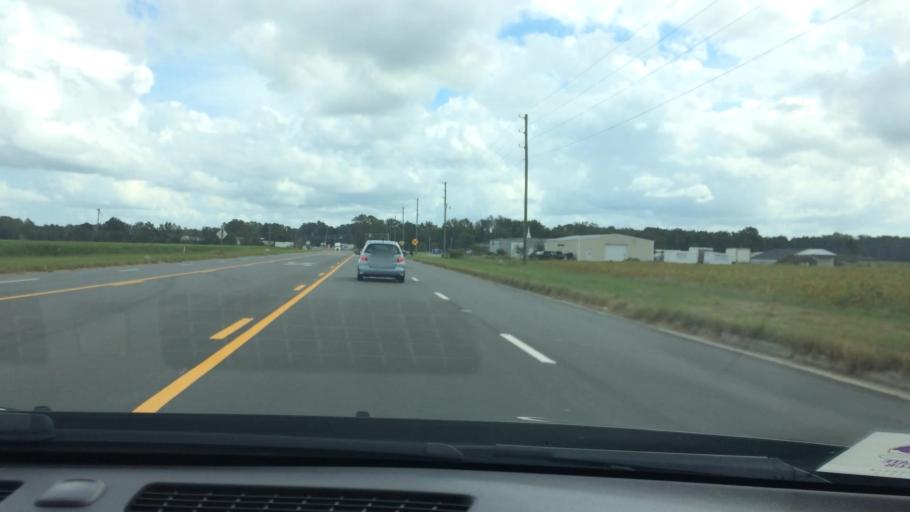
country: US
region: North Carolina
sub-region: Pitt County
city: Farmville
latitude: 35.5941
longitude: -77.6265
